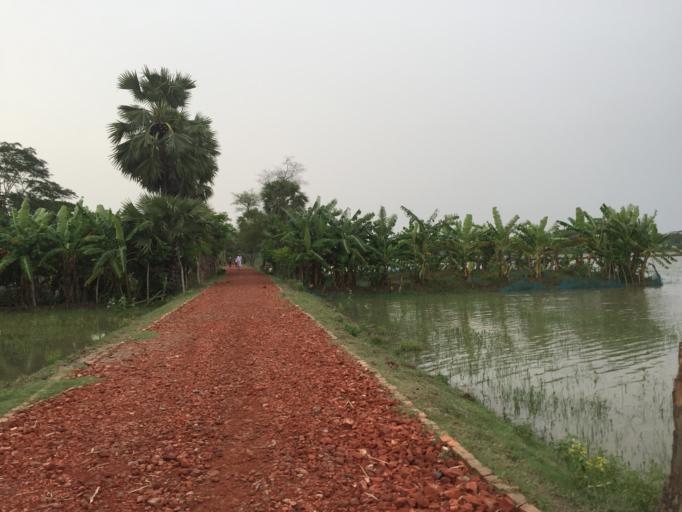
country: BD
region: Barisal
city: Mathba
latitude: 22.1930
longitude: 89.9317
